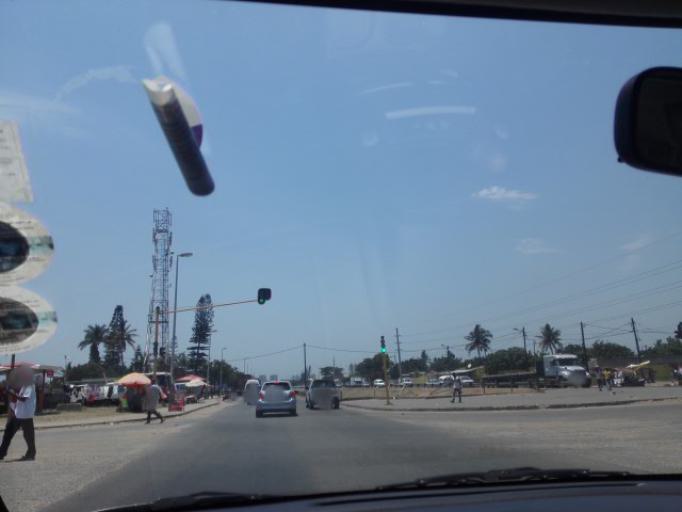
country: MZ
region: Maputo City
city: Maputo
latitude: -25.9377
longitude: 32.5666
